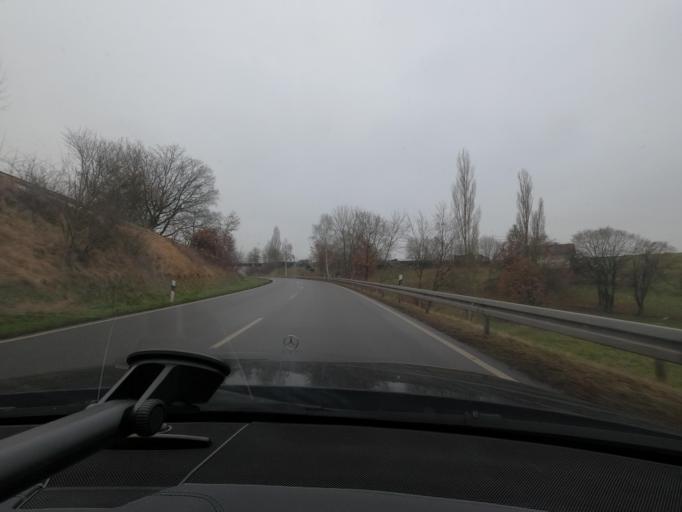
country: DE
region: Hesse
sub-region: Regierungsbezirk Kassel
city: Volkmarsen
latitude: 51.3449
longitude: 9.0899
